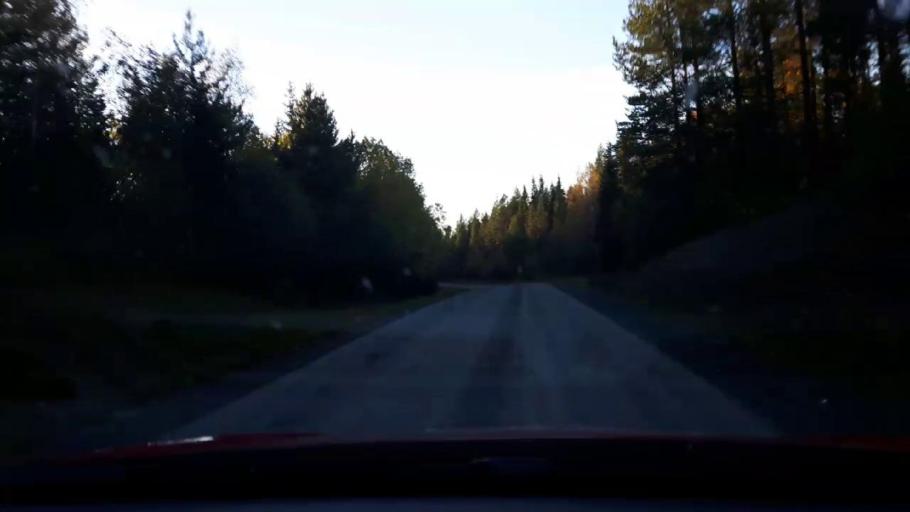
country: SE
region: Jaemtland
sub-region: Krokoms Kommun
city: Krokom
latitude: 63.4621
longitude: 14.3886
